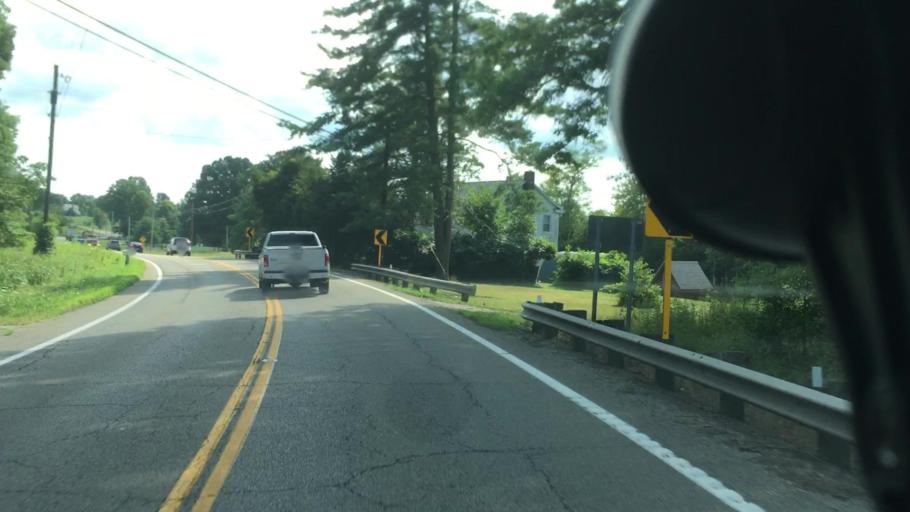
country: US
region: Ohio
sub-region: Mahoning County
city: Canfield
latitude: 40.9797
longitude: -80.8255
